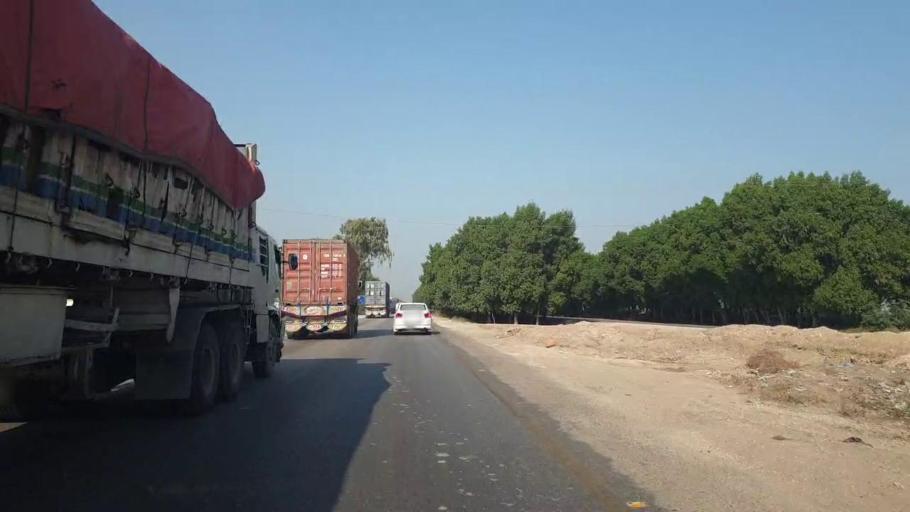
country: PK
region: Sindh
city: Matiari
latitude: 25.5157
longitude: 68.4297
